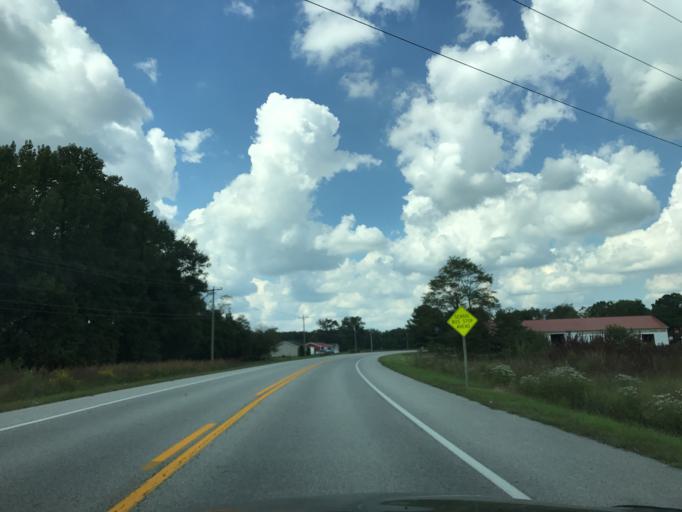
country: US
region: Maryland
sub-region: Caroline County
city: Greensboro
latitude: 39.1357
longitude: -75.8029
